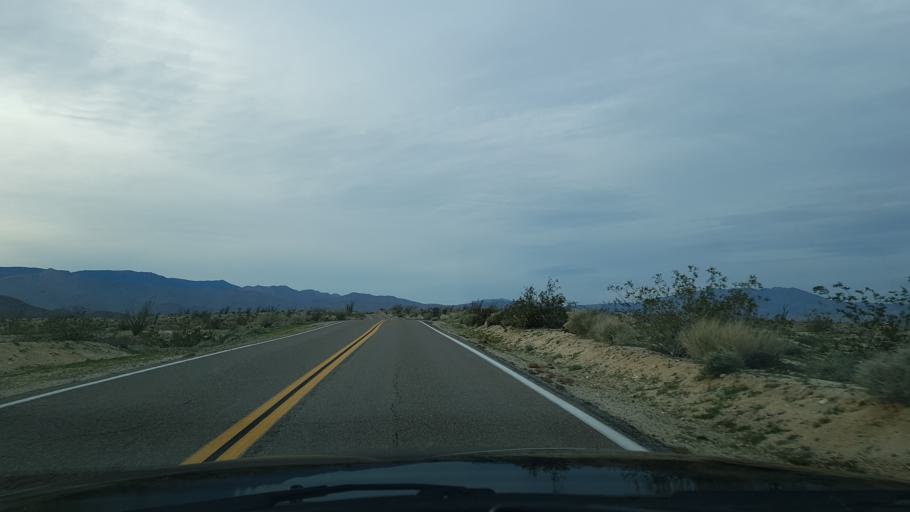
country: MX
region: Baja California
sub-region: Tecate
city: Cereso del Hongo
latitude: 32.8189
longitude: -116.1488
